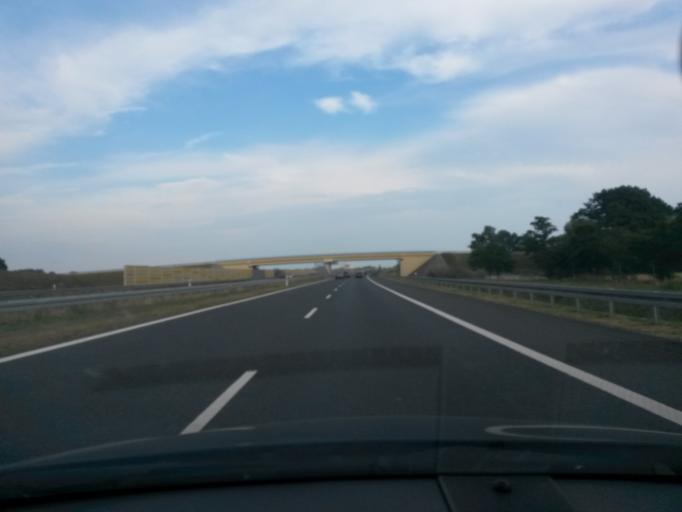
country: PL
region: Lodz Voivodeship
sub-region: Powiat poddebicki
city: Wartkowice
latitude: 51.9886
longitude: 19.0573
